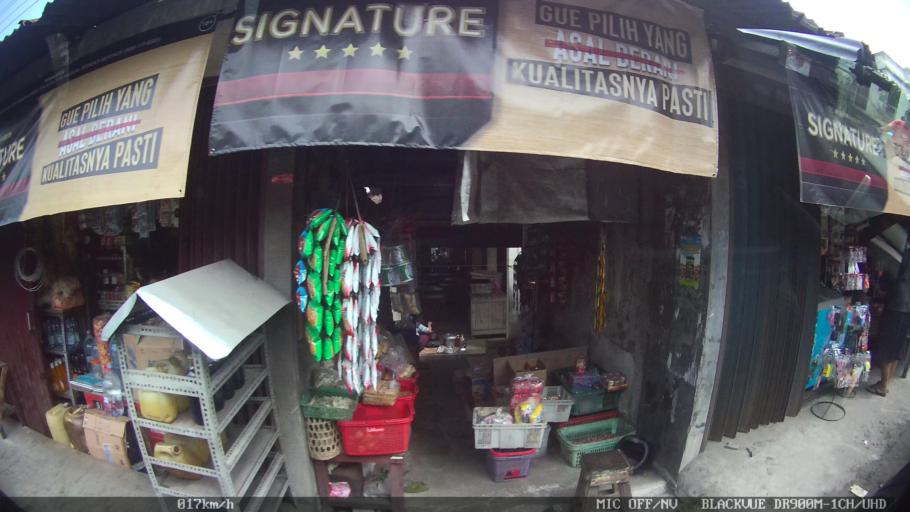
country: ID
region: Central Java
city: Candi Prambanan
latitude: -7.7364
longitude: 110.4813
